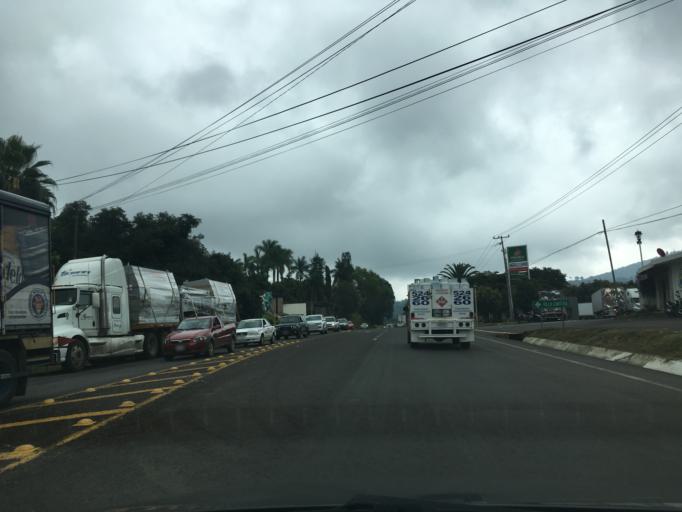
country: MX
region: Michoacan
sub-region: Uruapan
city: Toreo Bajo (El Toreo Bajo)
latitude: 19.4381
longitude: -102.0151
